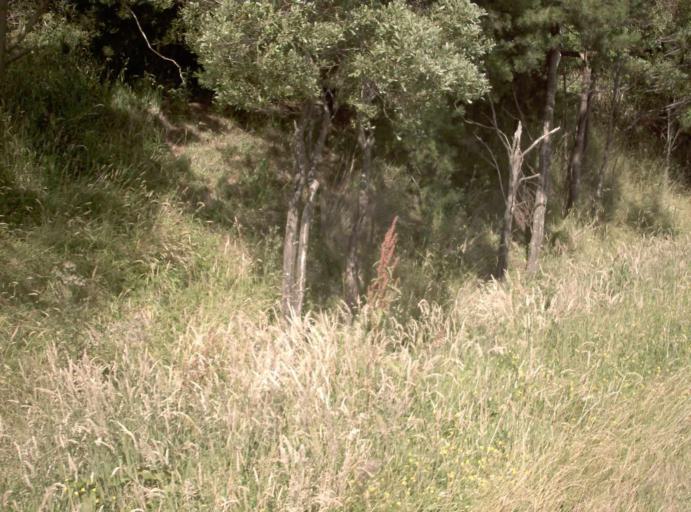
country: AU
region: Victoria
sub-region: Baw Baw
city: Warragul
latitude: -38.3732
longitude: 145.8398
